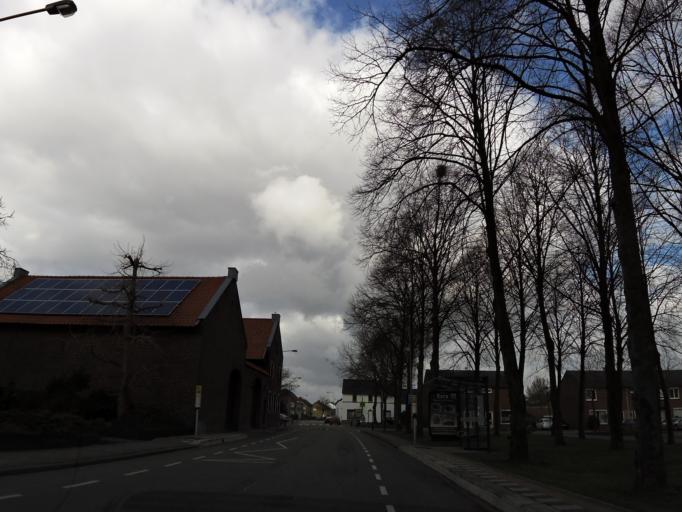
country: NL
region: Limburg
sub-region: Gemeente Stein
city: Berg
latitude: 51.0277
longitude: 5.7815
